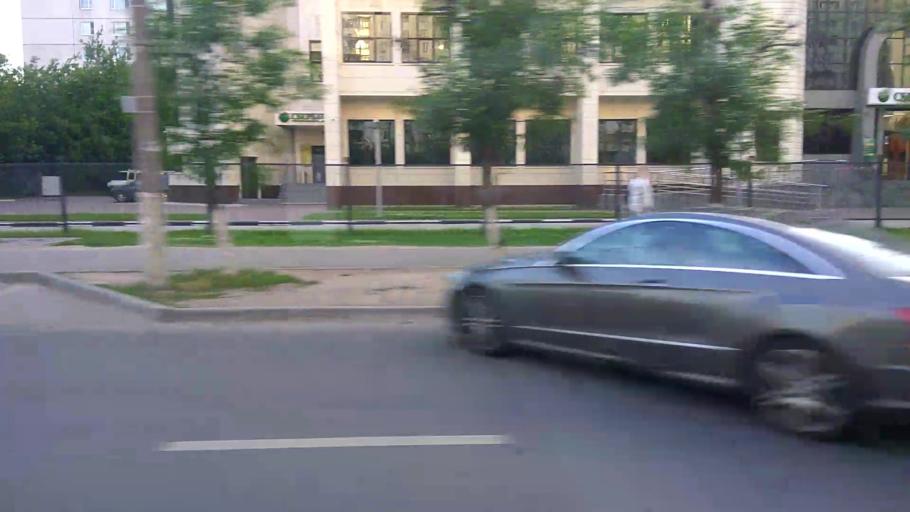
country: RU
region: Moskovskaya
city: Yubileyny
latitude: 55.9188
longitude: 37.8681
